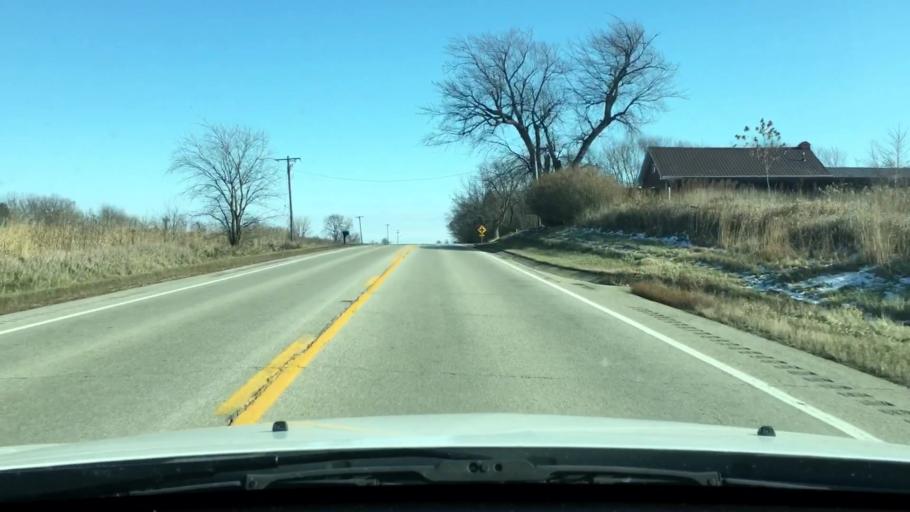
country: US
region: Illinois
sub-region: DeKalb County
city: Malta
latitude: 42.0009
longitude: -88.9019
